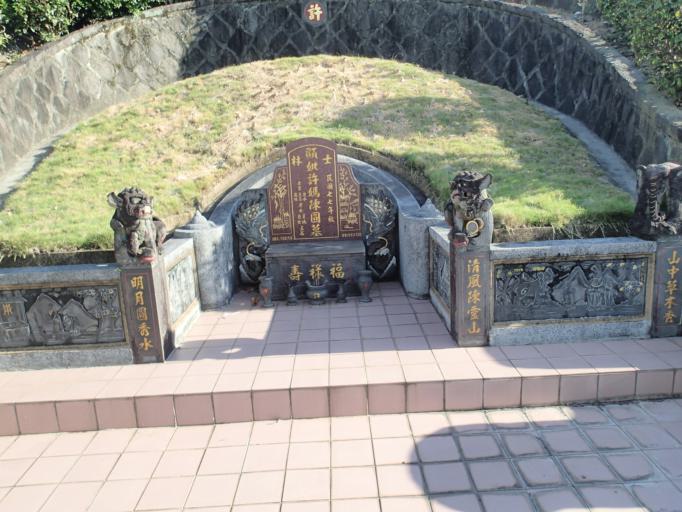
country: TW
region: Taipei
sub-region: Taipei
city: Banqiao
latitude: 25.1091
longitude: 121.4389
